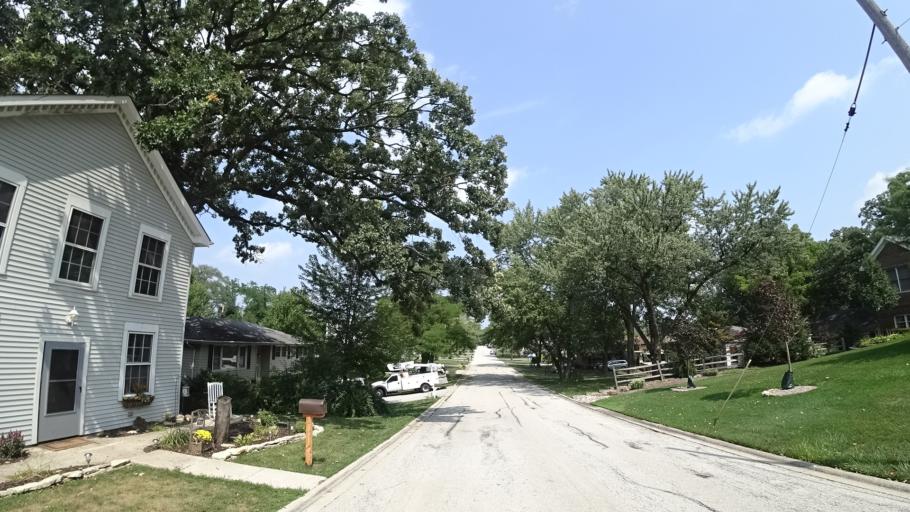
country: US
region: Illinois
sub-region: Cook County
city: Orland Park
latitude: 41.6267
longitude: -87.8658
